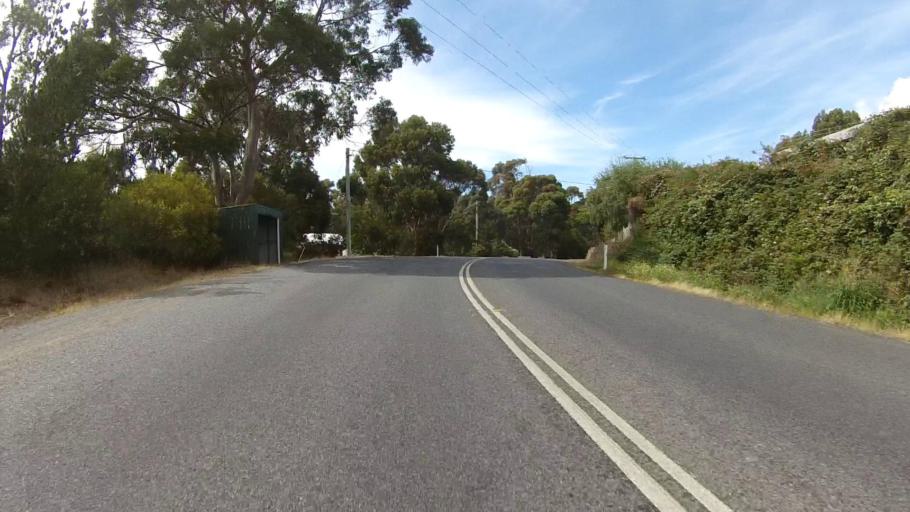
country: AU
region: Tasmania
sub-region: Kingborough
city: Kettering
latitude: -43.1486
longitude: 147.2395
